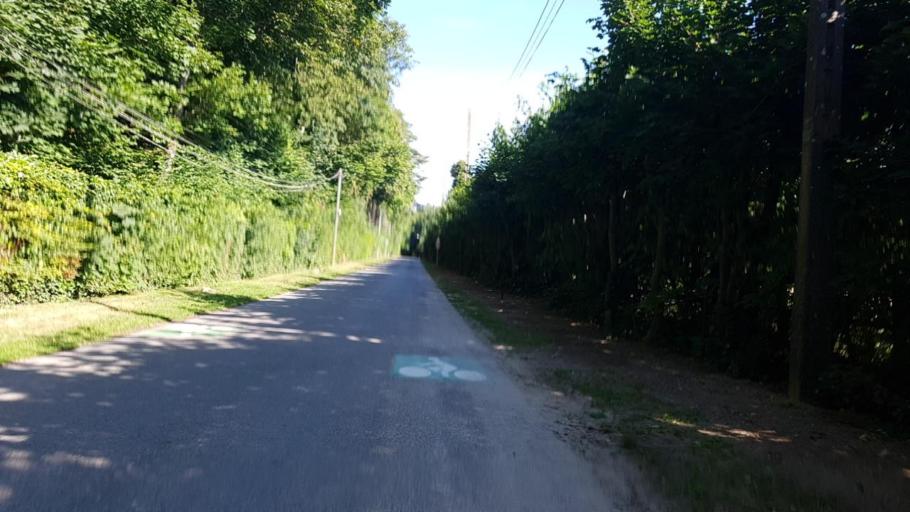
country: FR
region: Picardie
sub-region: Departement de l'Oise
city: Chamant
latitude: 49.2280
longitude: 2.6032
